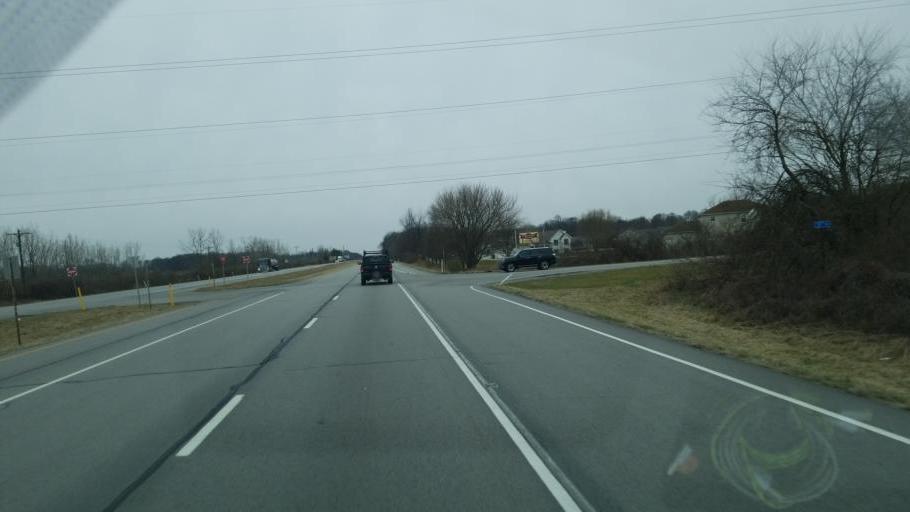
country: US
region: Indiana
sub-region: Marshall County
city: Plymouth
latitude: 41.3181
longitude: -86.2758
